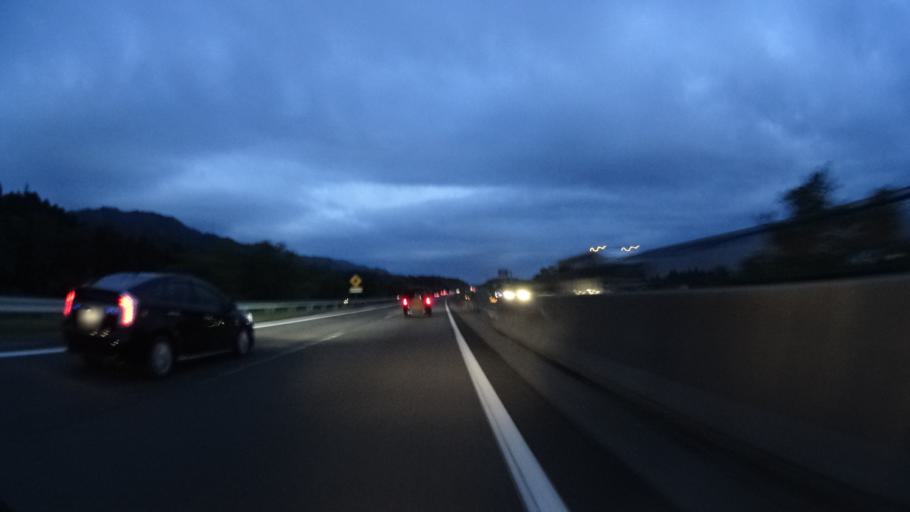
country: JP
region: Shiga Prefecture
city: Youkaichi
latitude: 35.1570
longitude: 136.2793
